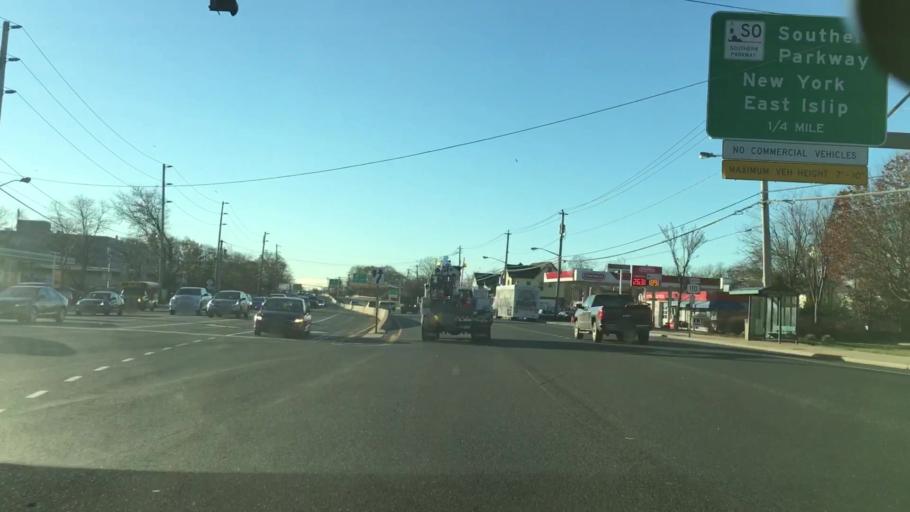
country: US
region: New York
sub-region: Suffolk County
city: North Amityville
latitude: 40.7107
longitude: -73.4289
